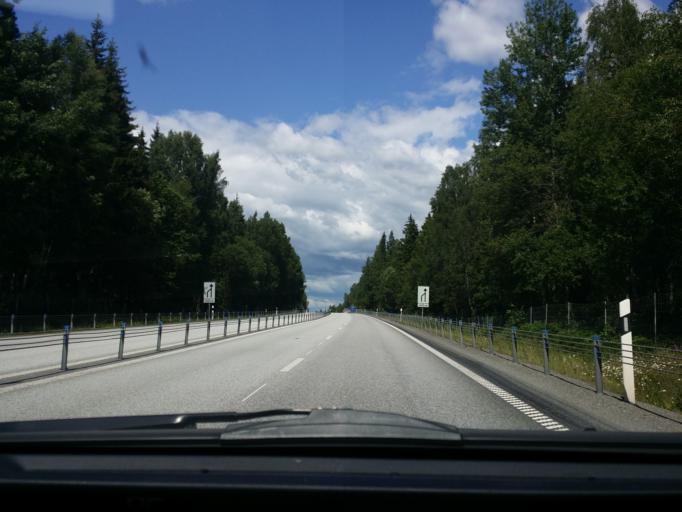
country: SE
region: OErebro
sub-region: Orebro Kommun
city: Hovsta
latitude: 59.3783
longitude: 15.2188
